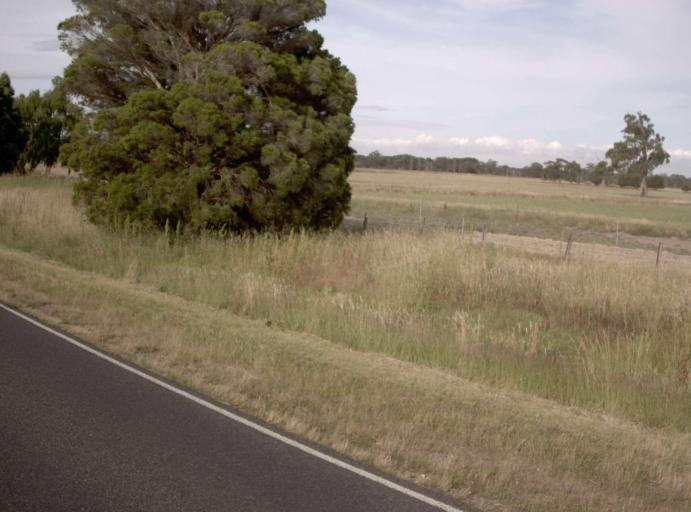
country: AU
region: Victoria
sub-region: Wellington
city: Heyfield
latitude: -38.0167
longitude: 146.6707
